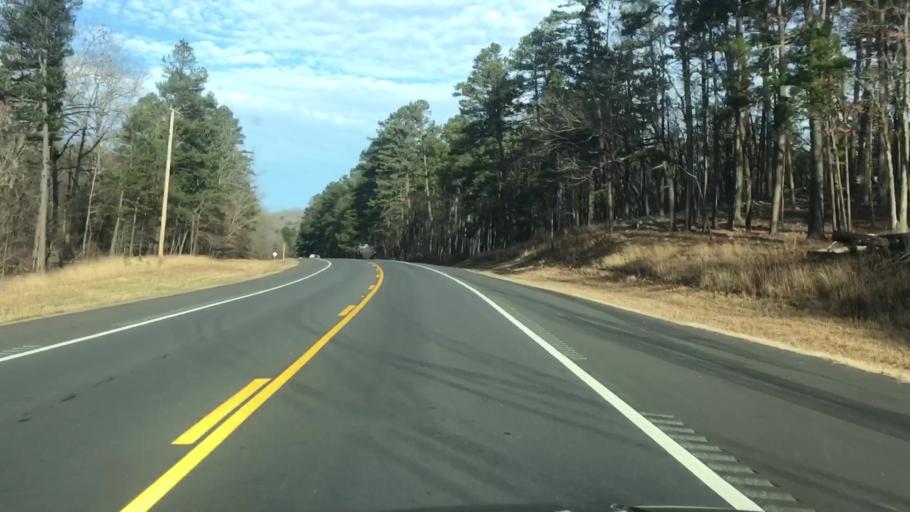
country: US
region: Arkansas
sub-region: Pike County
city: Glenwood
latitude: 34.5164
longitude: -93.3845
